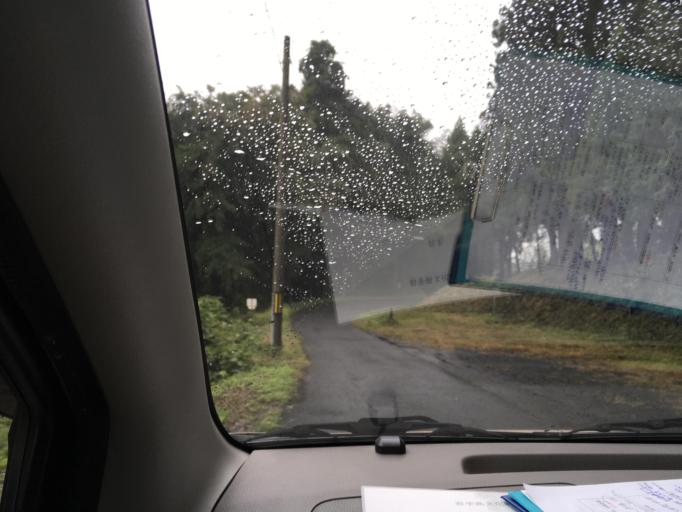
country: JP
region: Iwate
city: Ichinoseki
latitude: 38.8167
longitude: 141.1920
